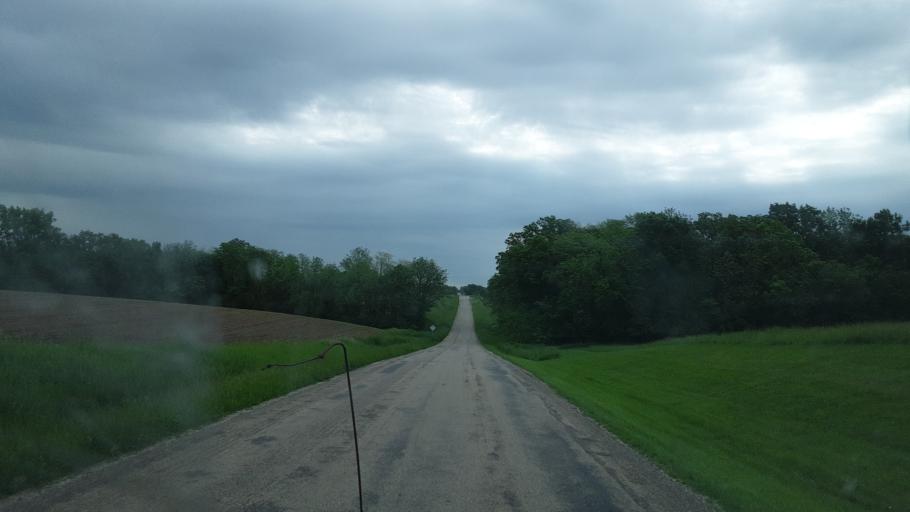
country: US
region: Illinois
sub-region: Fulton County
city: Astoria
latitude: 40.3643
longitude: -90.4546
